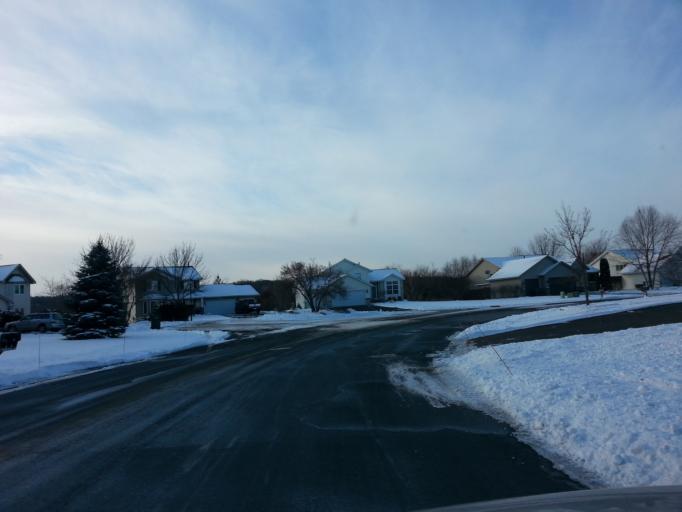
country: US
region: Minnesota
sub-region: Scott County
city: Savage
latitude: 44.7751
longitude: -93.3943
